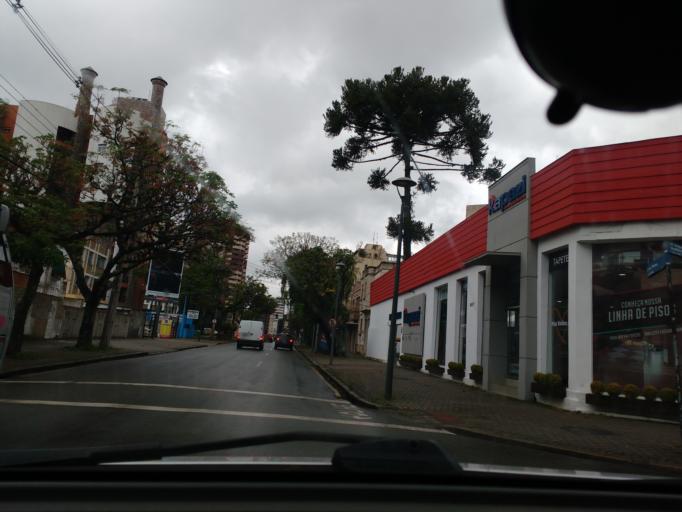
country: BR
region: Parana
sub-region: Curitiba
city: Curitiba
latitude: -25.4321
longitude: -49.2847
